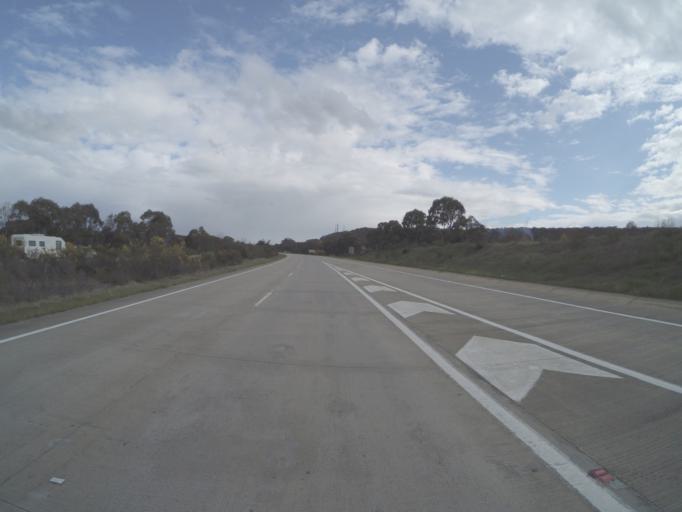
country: AU
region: New South Wales
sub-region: Goulburn Mulwaree
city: Goulburn
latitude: -34.7445
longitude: 149.7701
